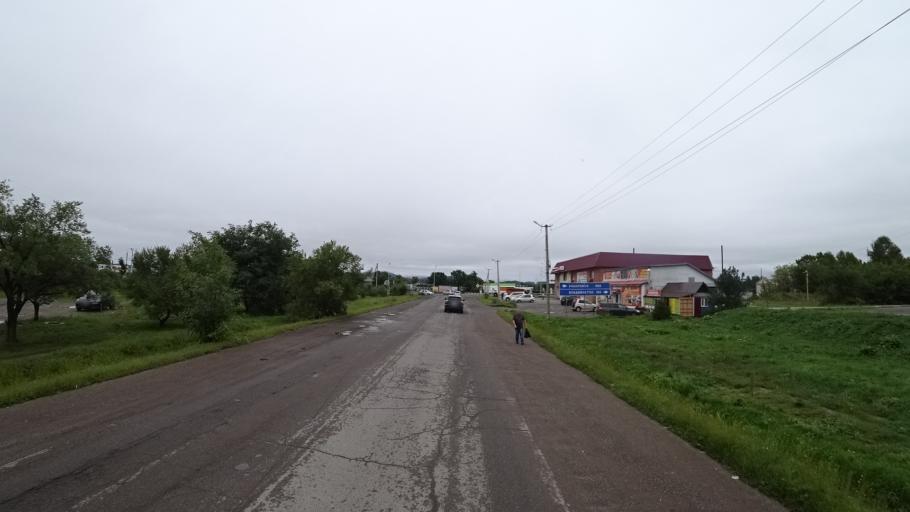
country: RU
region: Primorskiy
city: Monastyrishche
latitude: 44.2034
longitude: 132.4489
